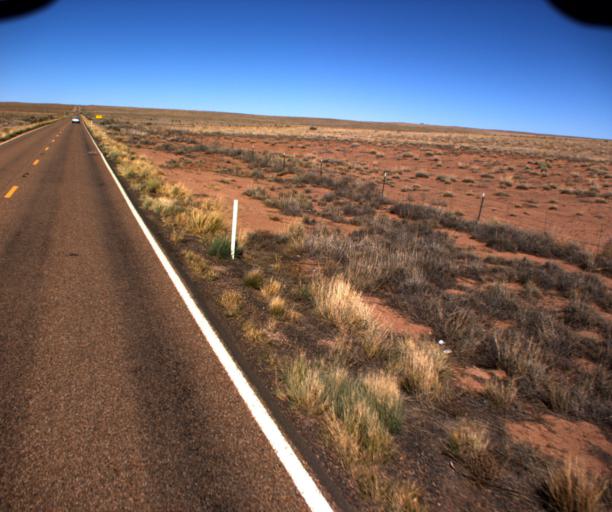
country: US
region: Arizona
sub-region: Navajo County
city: Holbrook
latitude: 34.9804
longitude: -110.0886
